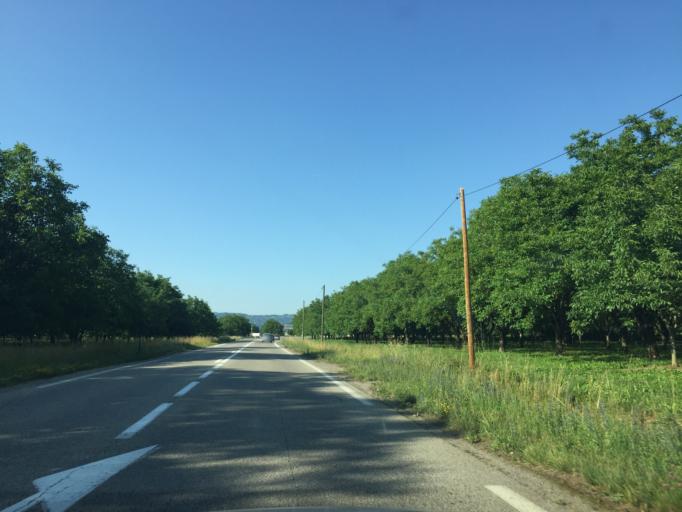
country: FR
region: Rhone-Alpes
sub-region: Departement de l'Isere
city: Saint-Sauveur
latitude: 45.1515
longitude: 5.3786
